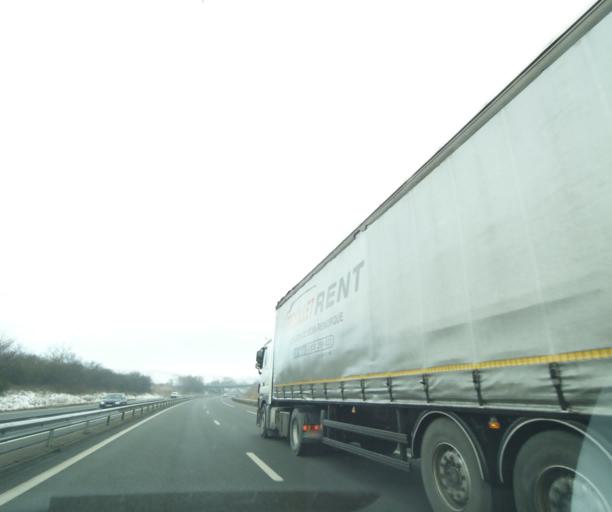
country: FR
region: Auvergne
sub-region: Departement du Puy-de-Dome
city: Saint-Bonnet-pres-Riom
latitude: 45.9519
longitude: 3.1102
